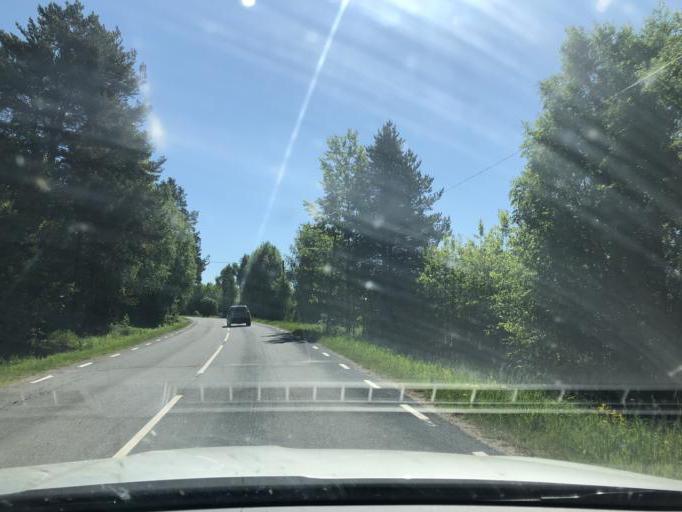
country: SE
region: Norrbotten
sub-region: Lulea Kommun
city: Gammelstad
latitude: 65.6574
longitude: 21.9979
